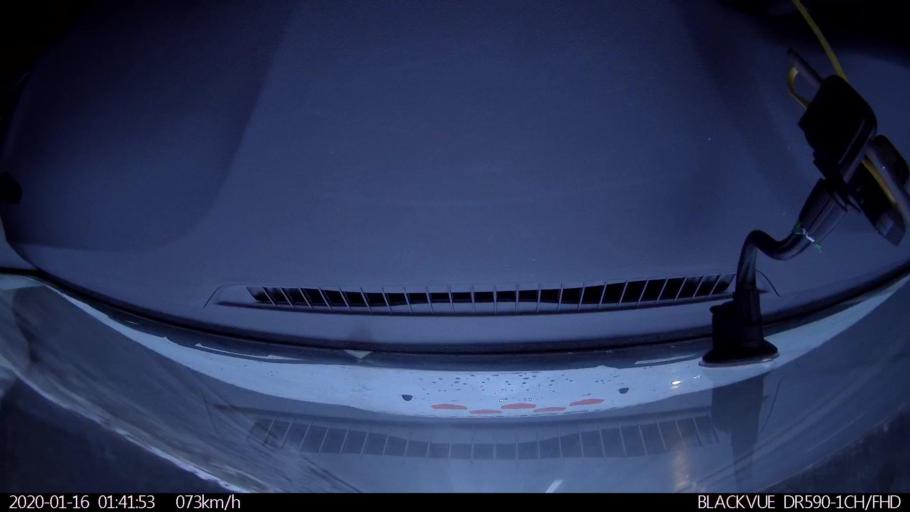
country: RU
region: Nizjnij Novgorod
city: Gorbatovka
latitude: 56.3176
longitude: 43.7592
